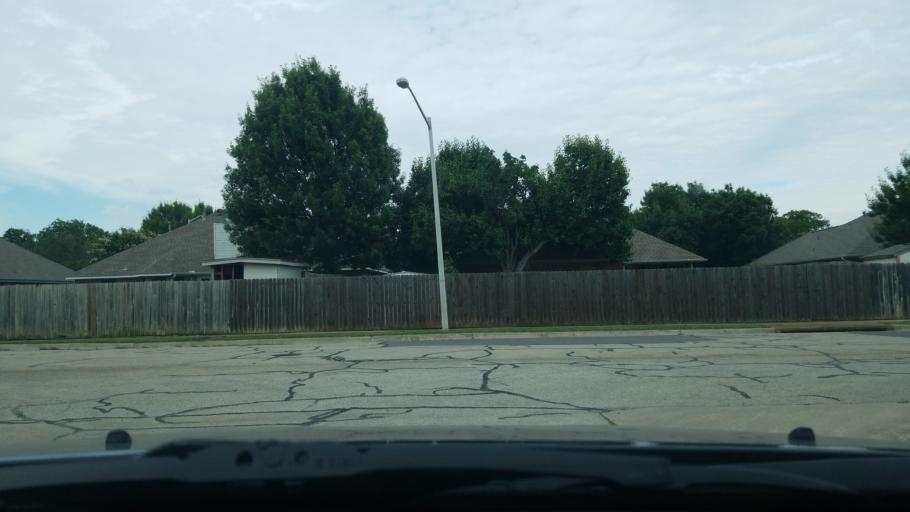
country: US
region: Texas
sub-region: Denton County
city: Denton
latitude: 33.2461
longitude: -97.1275
